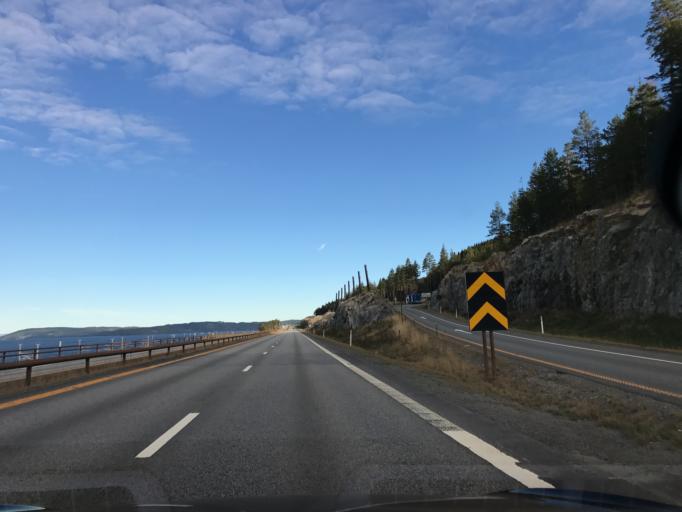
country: NO
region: Akershus
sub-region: Eidsvoll
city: Eidsvoll
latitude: 60.5268
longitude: 11.2430
